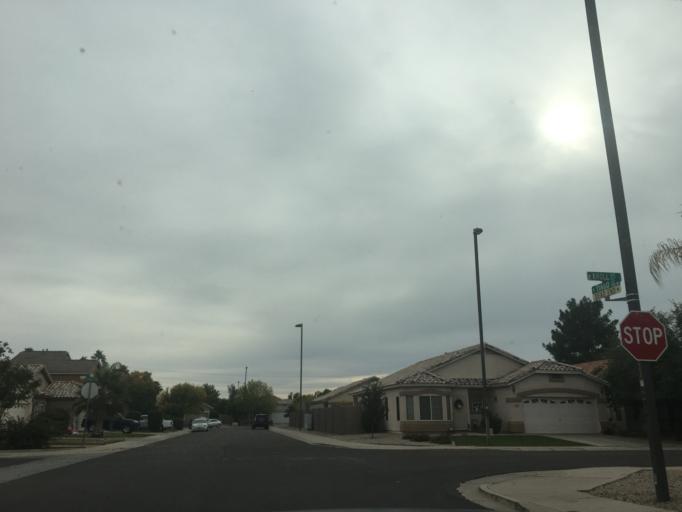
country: US
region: Arizona
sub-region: Maricopa County
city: Gilbert
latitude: 33.3611
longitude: -111.8078
